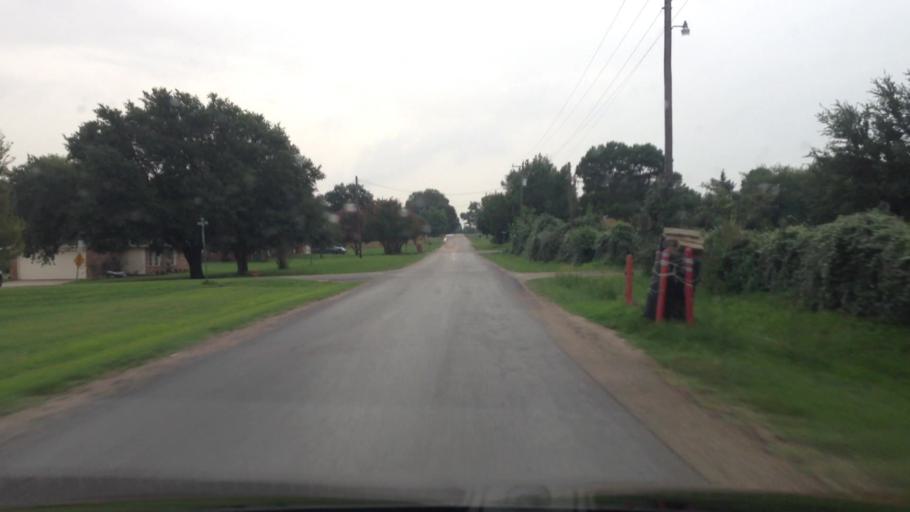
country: US
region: Texas
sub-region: Johnson County
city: Joshua
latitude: 32.4820
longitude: -97.3435
